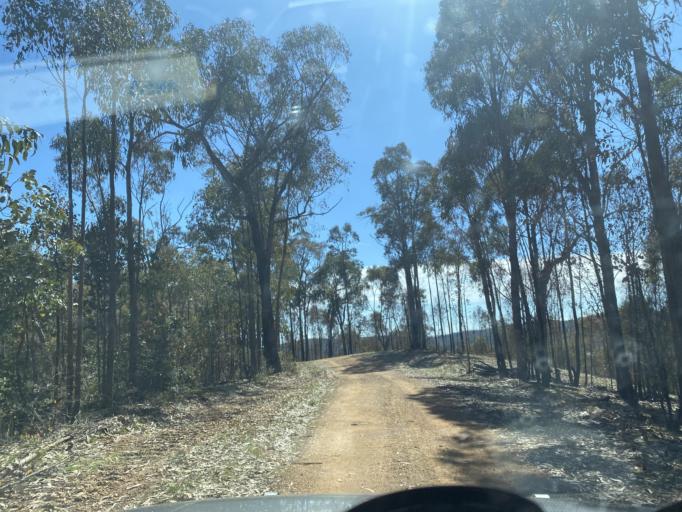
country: AU
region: Victoria
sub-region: Benalla
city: Benalla
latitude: -36.7334
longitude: 146.1828
